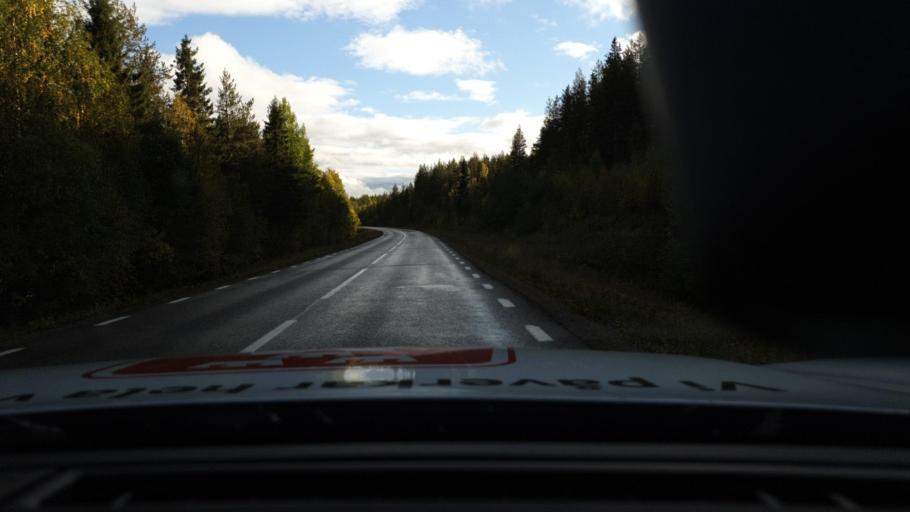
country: SE
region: Norrbotten
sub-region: Overkalix Kommun
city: OEverkalix
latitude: 66.7481
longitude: 22.6710
